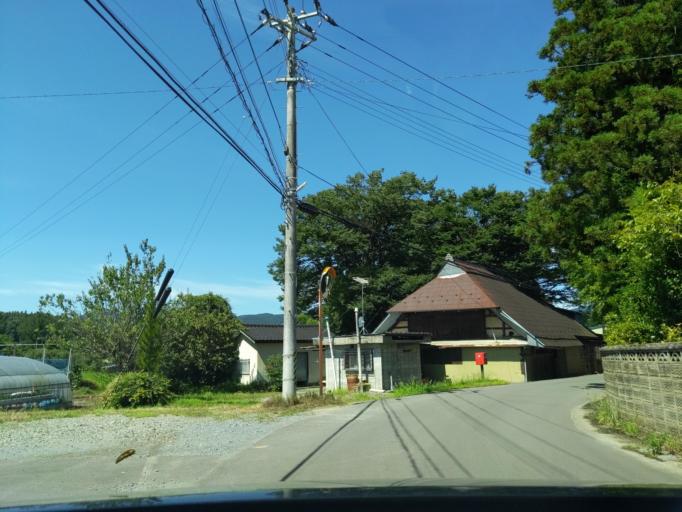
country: JP
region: Fukushima
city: Koriyama
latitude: 37.3646
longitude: 140.2818
